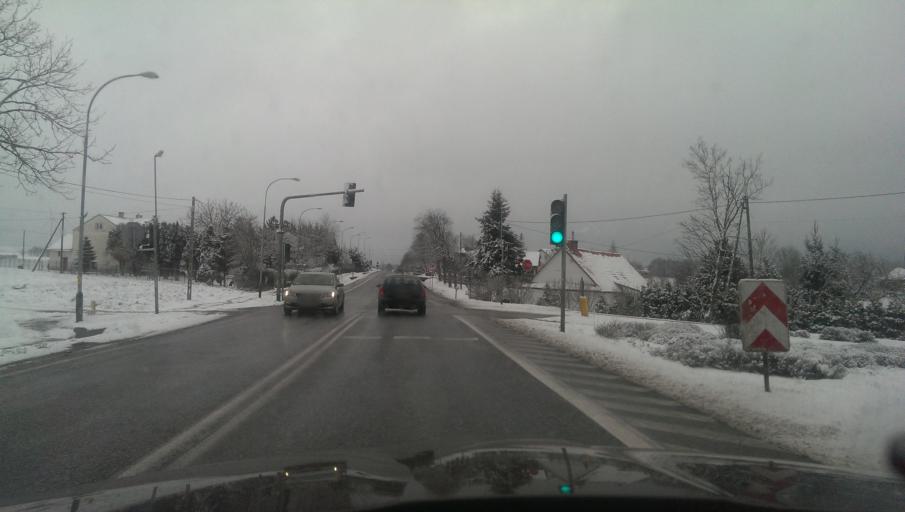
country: PL
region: Subcarpathian Voivodeship
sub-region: Powiat krosnienski
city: Miejsce Piastowe
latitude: 49.6051
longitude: 21.8068
